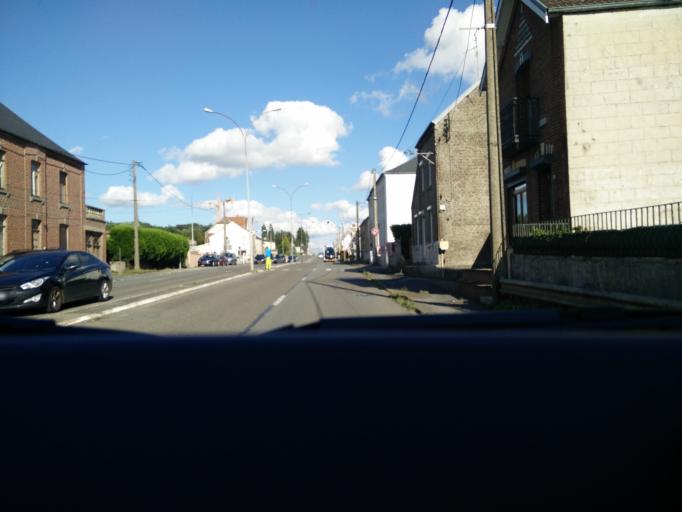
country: FR
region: Nord-Pas-de-Calais
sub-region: Departement du Nord
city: Feignies
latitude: 50.2808
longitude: 3.9311
